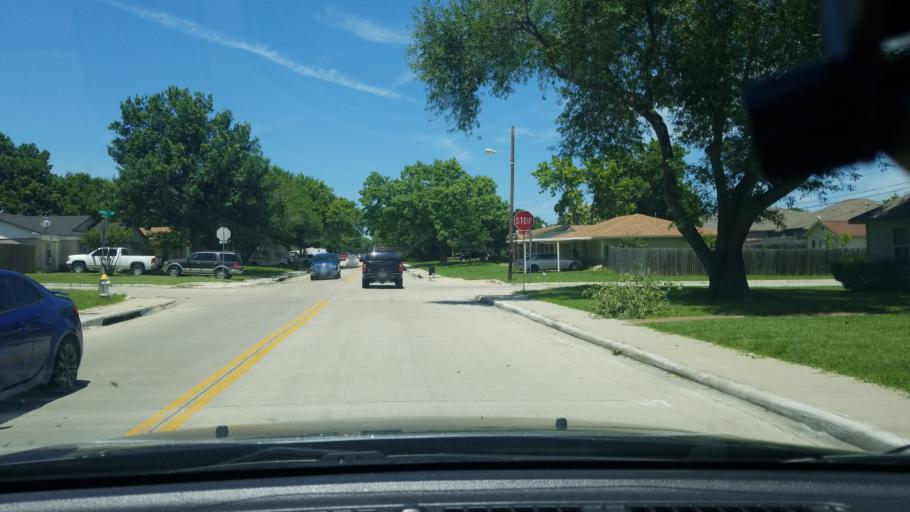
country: US
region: Texas
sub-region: Dallas County
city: Mesquite
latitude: 32.7826
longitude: -96.6205
